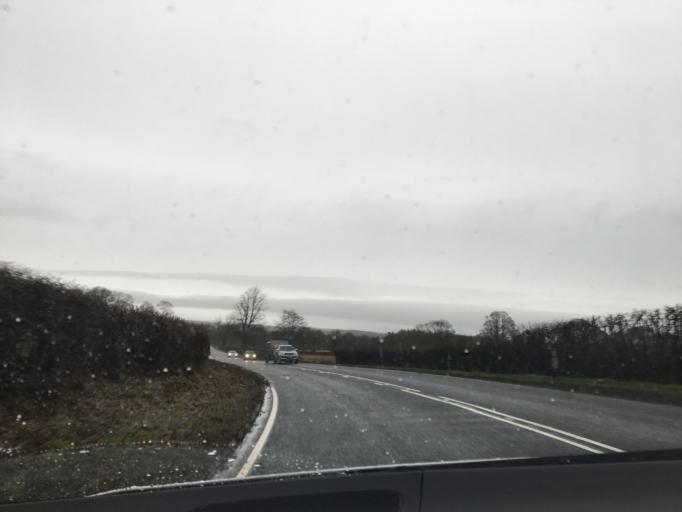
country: GB
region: Scotland
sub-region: Stirling
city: Doune
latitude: 56.1736
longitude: -4.0640
